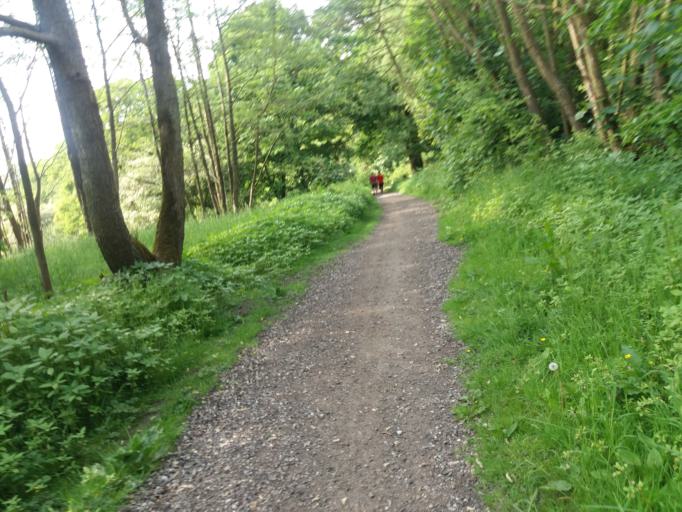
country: GB
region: England
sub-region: Lancashire
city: Coppull
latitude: 53.6486
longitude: -2.6568
